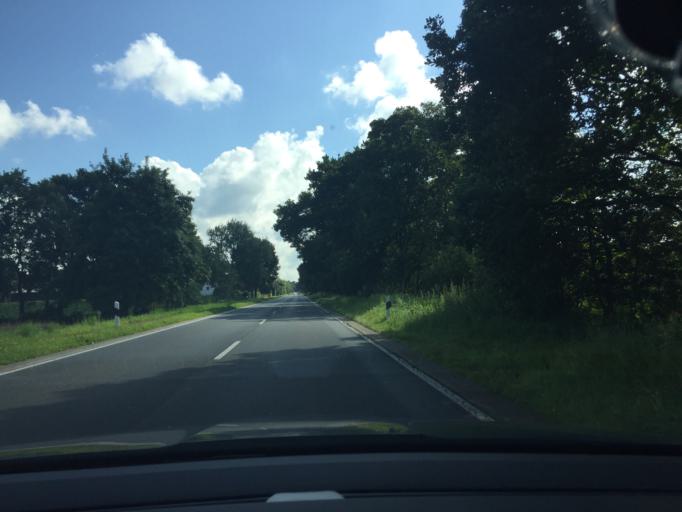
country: DE
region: Lower Saxony
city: Aurich
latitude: 53.5069
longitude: 7.5192
